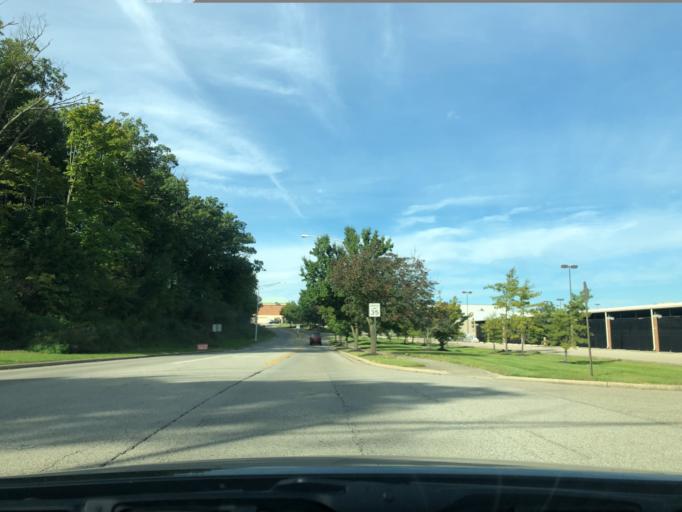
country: US
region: Ohio
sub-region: Hamilton County
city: Glendale
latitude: 39.2838
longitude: -84.4631
